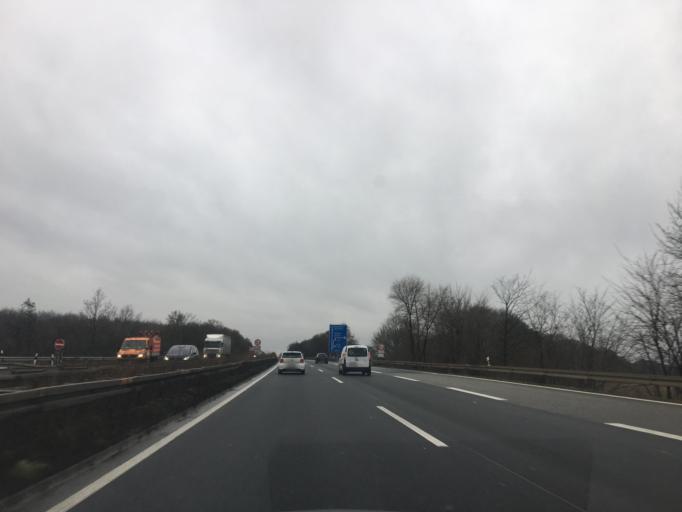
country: DE
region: North Rhine-Westphalia
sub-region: Regierungsbezirk Dusseldorf
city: Viersen
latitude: 51.2189
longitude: 6.4021
